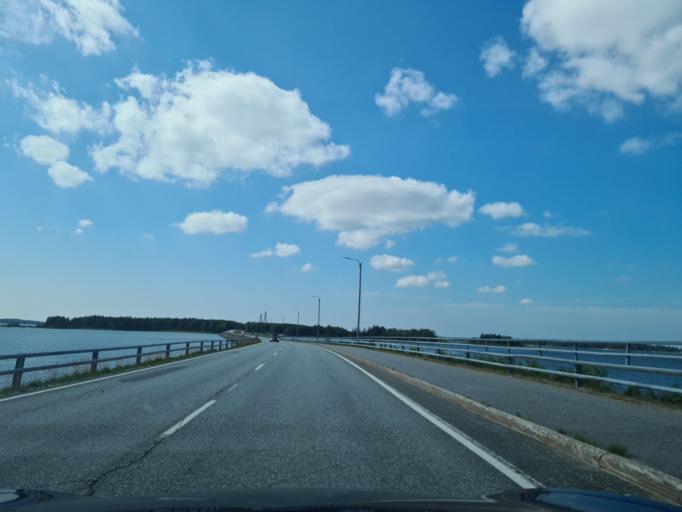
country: FI
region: Ostrobothnia
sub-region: Vaasa
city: Replot
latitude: 63.2054
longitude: 21.5162
